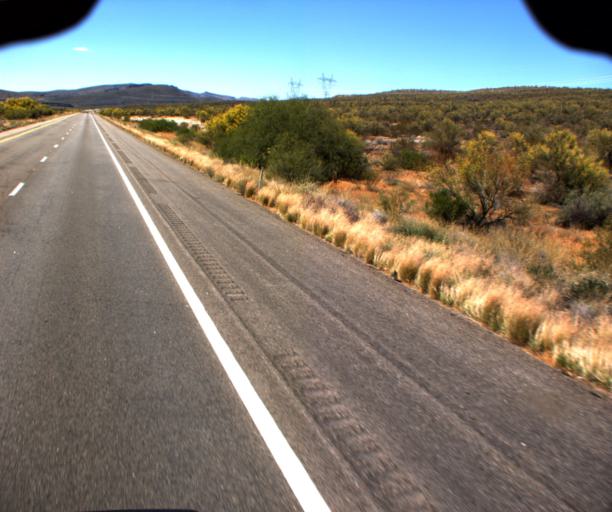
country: US
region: Arizona
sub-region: Yavapai County
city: Bagdad
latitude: 34.5213
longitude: -113.4234
